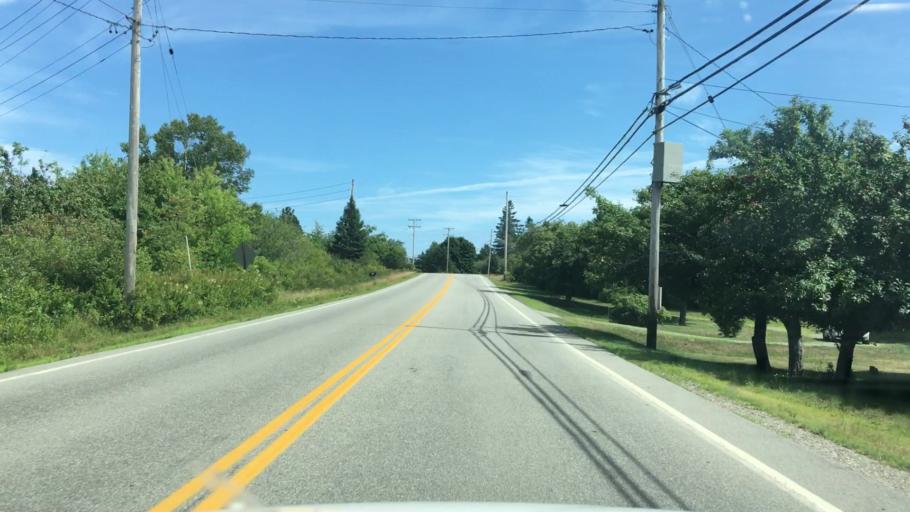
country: US
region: Maine
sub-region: Washington County
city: Eastport
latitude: 44.9136
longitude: -67.0053
